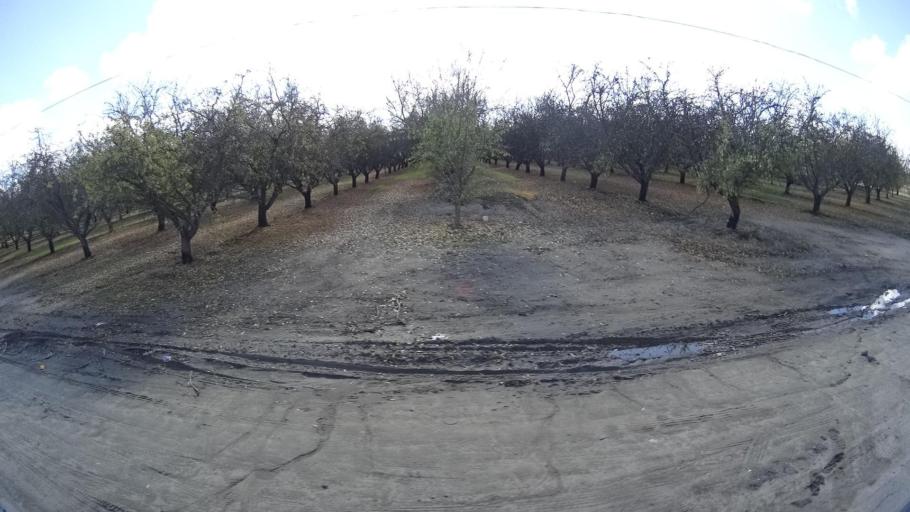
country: US
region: California
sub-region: Kern County
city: Wasco
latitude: 35.6887
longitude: -119.3299
